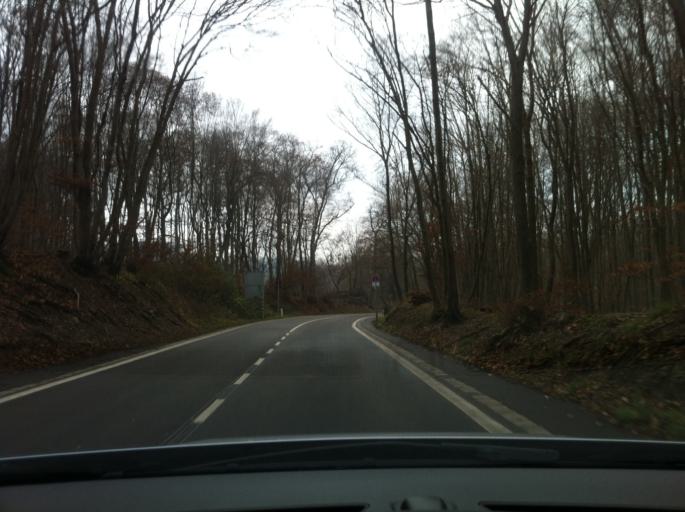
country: AT
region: Lower Austria
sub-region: Politischer Bezirk Wien-Umgebung
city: Klosterneuburg
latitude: 48.2409
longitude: 16.2748
